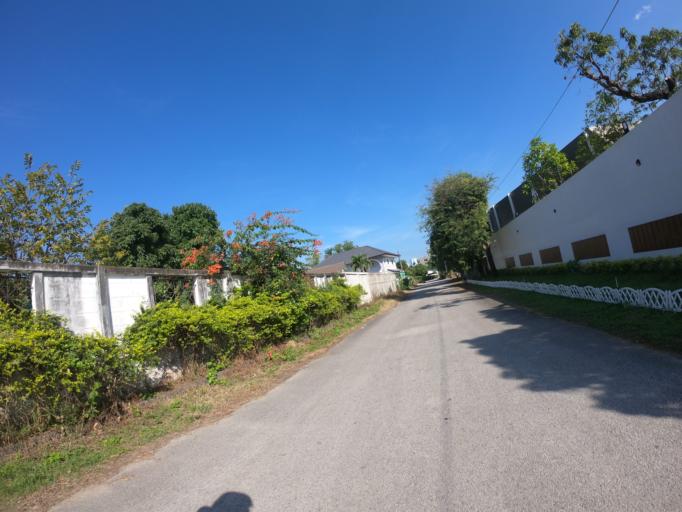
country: TH
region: Chiang Mai
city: Chiang Mai
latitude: 18.8084
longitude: 98.9889
